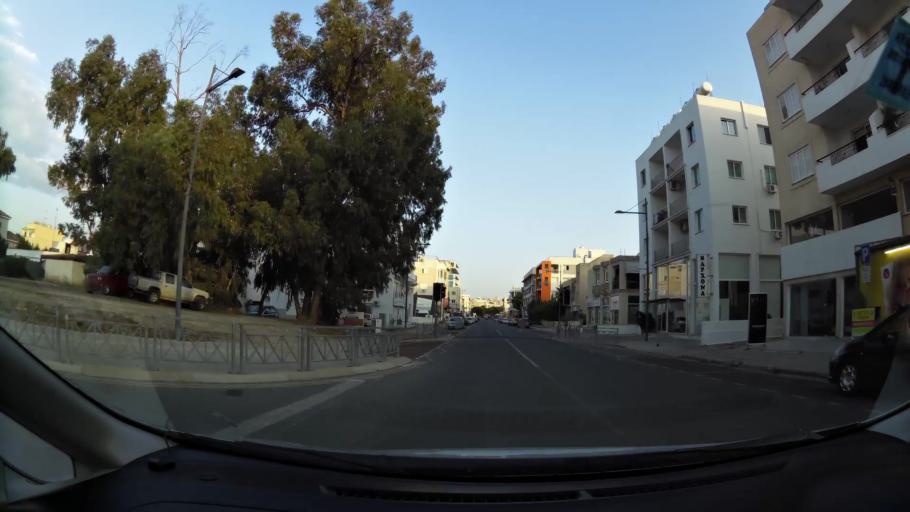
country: CY
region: Lefkosia
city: Nicosia
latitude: 35.1584
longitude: 33.3117
